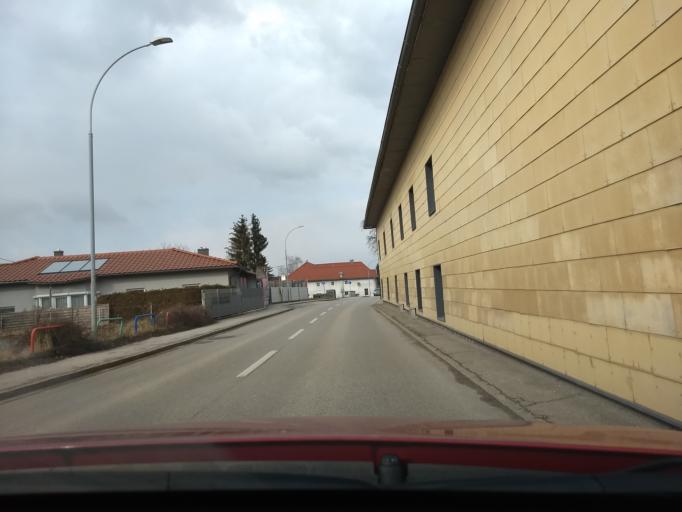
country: AT
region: Lower Austria
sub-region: Politischer Bezirk Amstetten
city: Haidershofen
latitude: 48.0719
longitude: 14.4240
